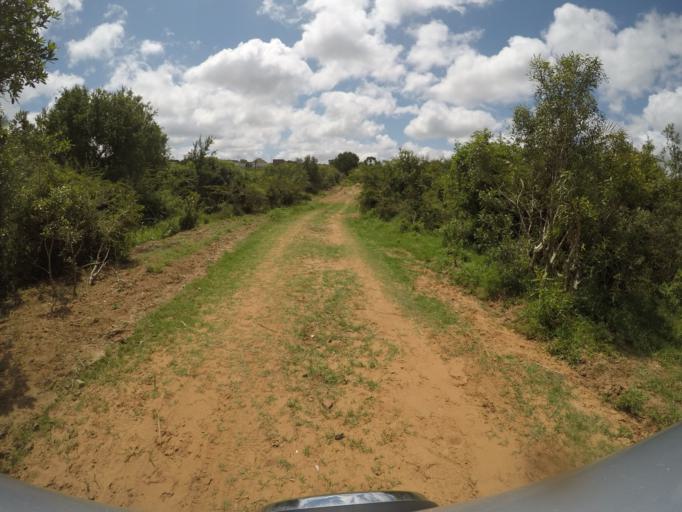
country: ZA
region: KwaZulu-Natal
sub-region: uThungulu District Municipality
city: Empangeni
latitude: -28.5848
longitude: 31.8422
